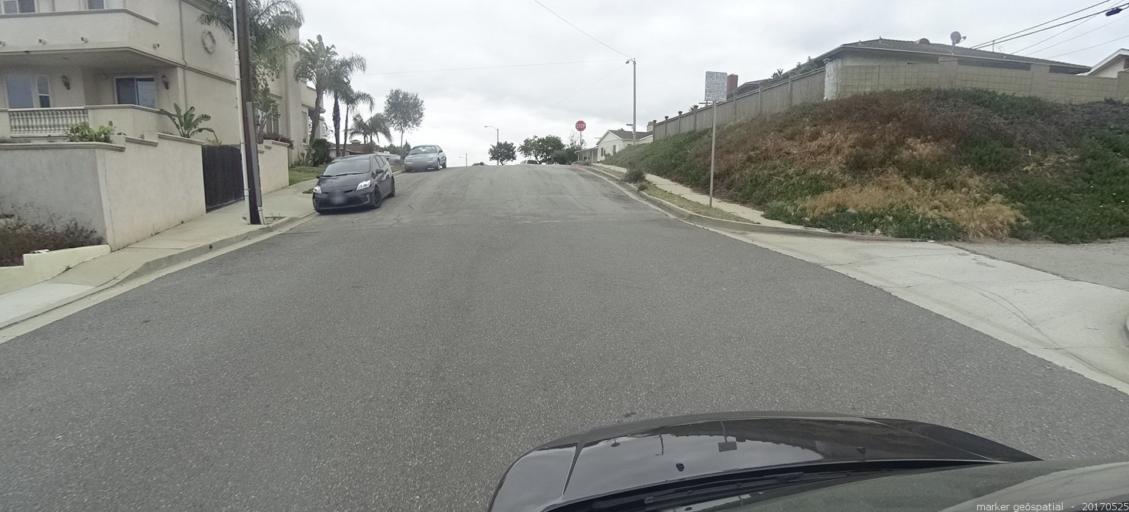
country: US
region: California
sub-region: Los Angeles County
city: Redondo Beach
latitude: 33.8459
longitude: -118.3768
